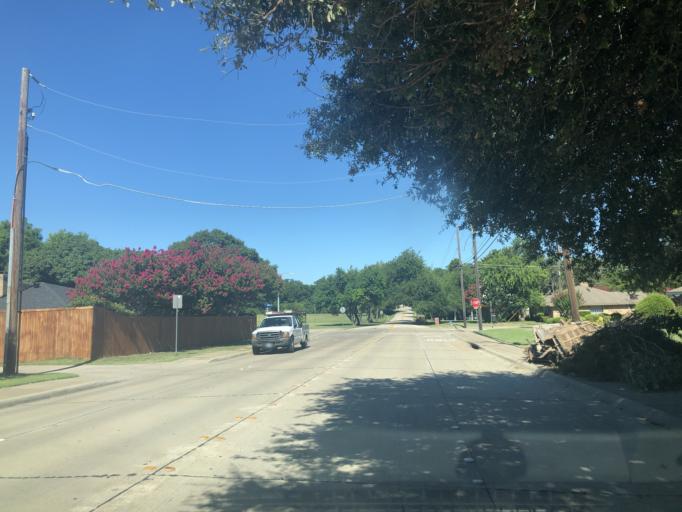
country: US
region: Texas
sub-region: Dallas County
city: Duncanville
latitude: 32.6556
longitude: -96.9318
